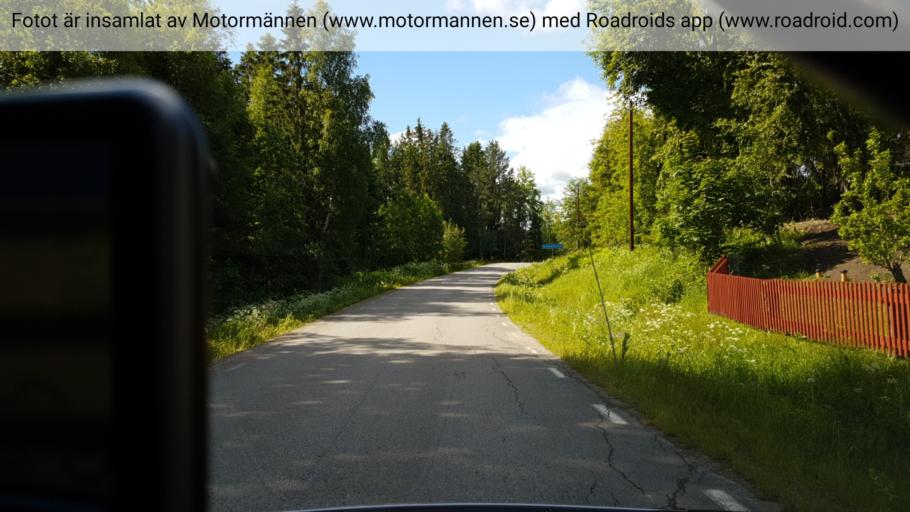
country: SE
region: Gaevleborg
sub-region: Hudiksvalls Kommun
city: Sorforsa
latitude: 61.6810
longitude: 16.9256
